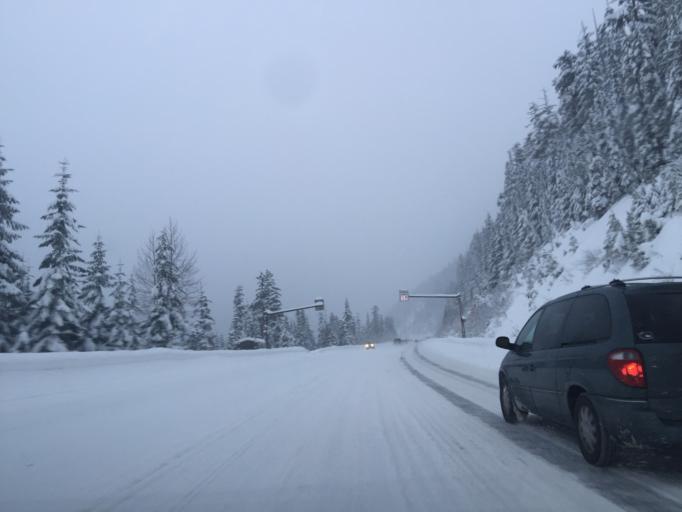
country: US
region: Washington
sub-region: Chelan County
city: Leavenworth
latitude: 47.7318
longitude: -121.1348
